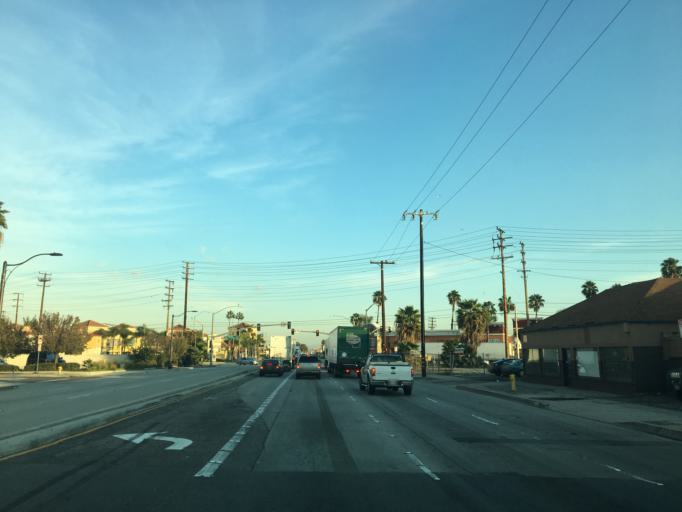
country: US
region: California
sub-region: Los Angeles County
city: Commerce
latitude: 34.0034
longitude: -118.1690
